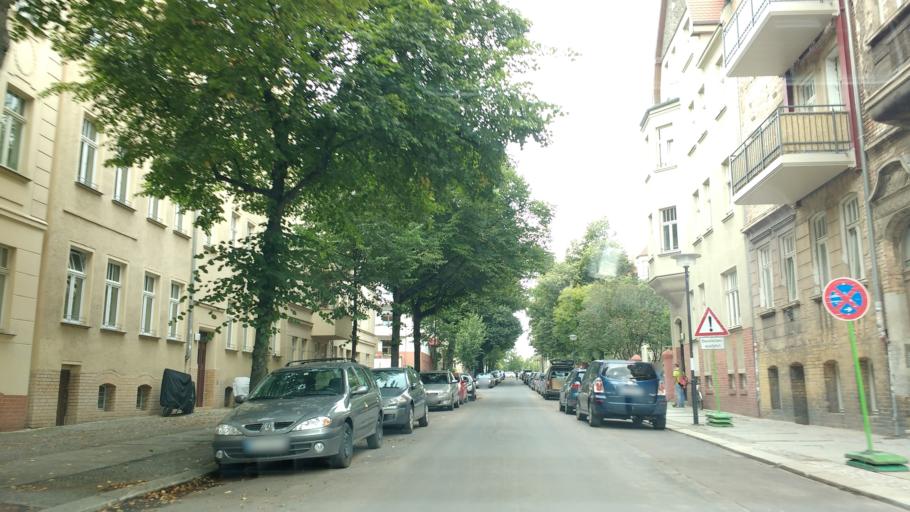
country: DE
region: Saxony-Anhalt
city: Halle (Saale)
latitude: 51.4951
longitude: 11.9794
